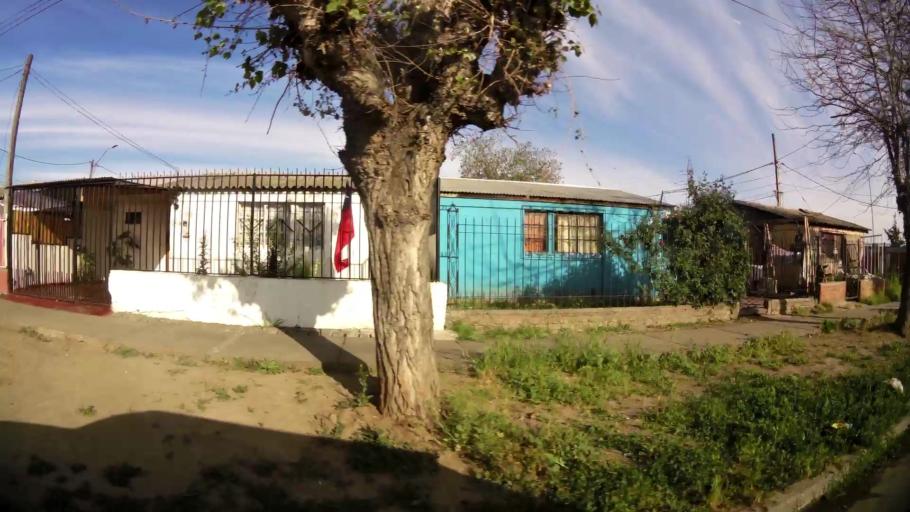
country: CL
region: Santiago Metropolitan
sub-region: Provincia de Santiago
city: Lo Prado
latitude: -33.4784
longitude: -70.7020
